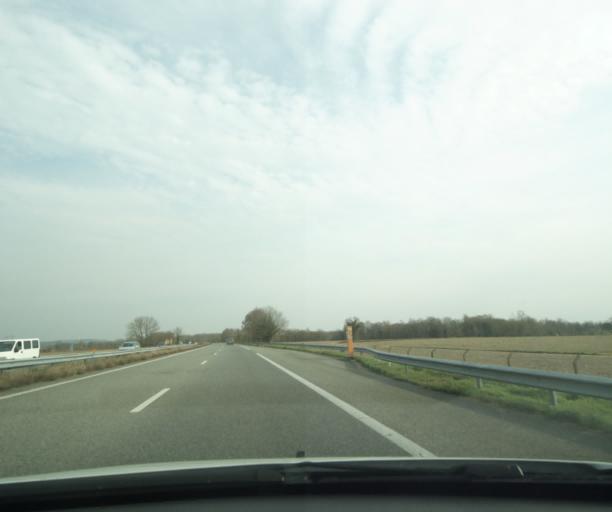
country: FR
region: Aquitaine
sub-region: Departement des Pyrenees-Atlantiques
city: Mont
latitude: 43.4276
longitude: -0.6238
